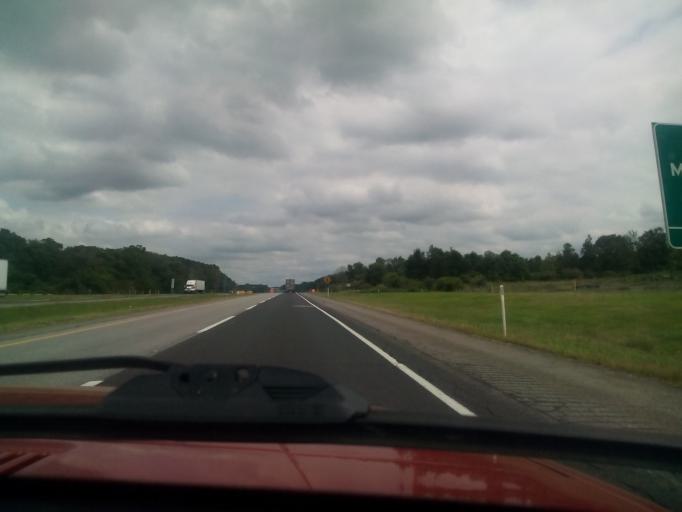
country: US
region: Indiana
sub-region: LaPorte County
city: Westville
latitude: 41.5862
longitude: -86.9251
